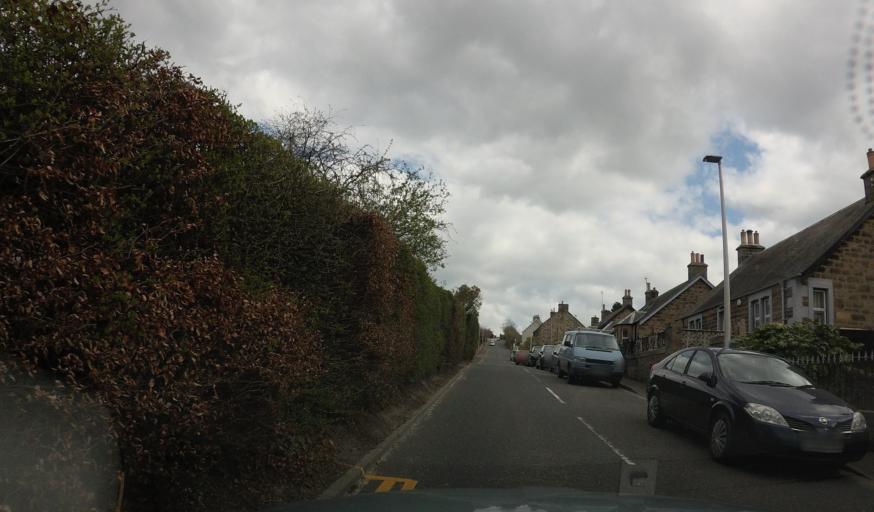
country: GB
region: Scotland
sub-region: Midlothian
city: Gorebridge
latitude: 55.8406
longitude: -3.0433
